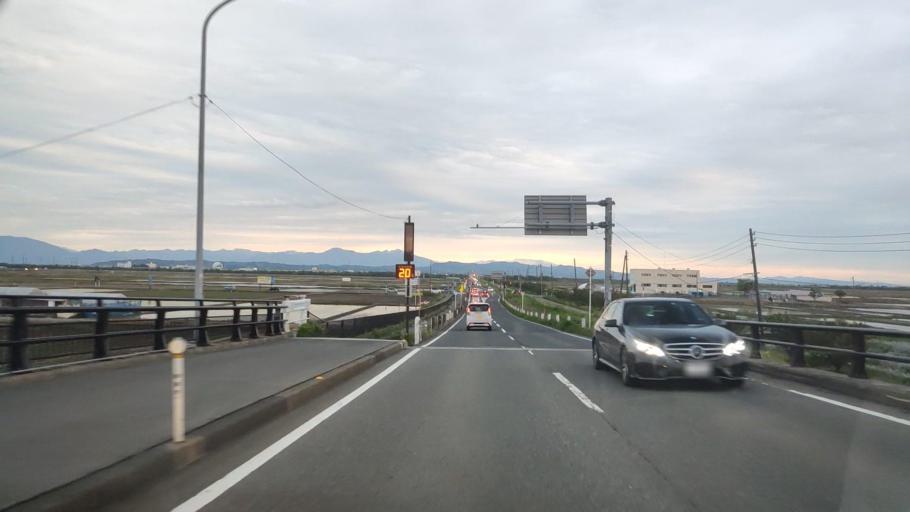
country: JP
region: Niigata
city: Kameda-honcho
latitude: 37.8343
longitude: 139.0965
